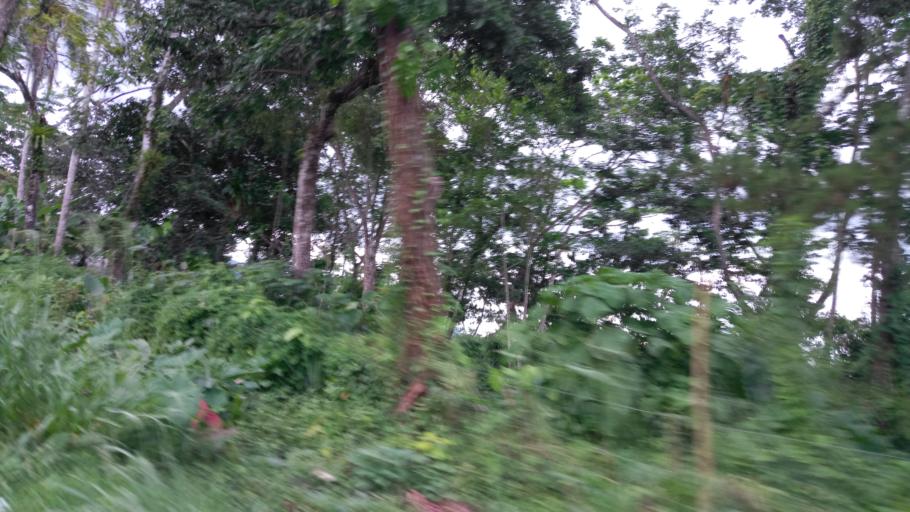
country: CR
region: Alajuela
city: Pocosol
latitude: 10.3740
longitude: -84.5633
